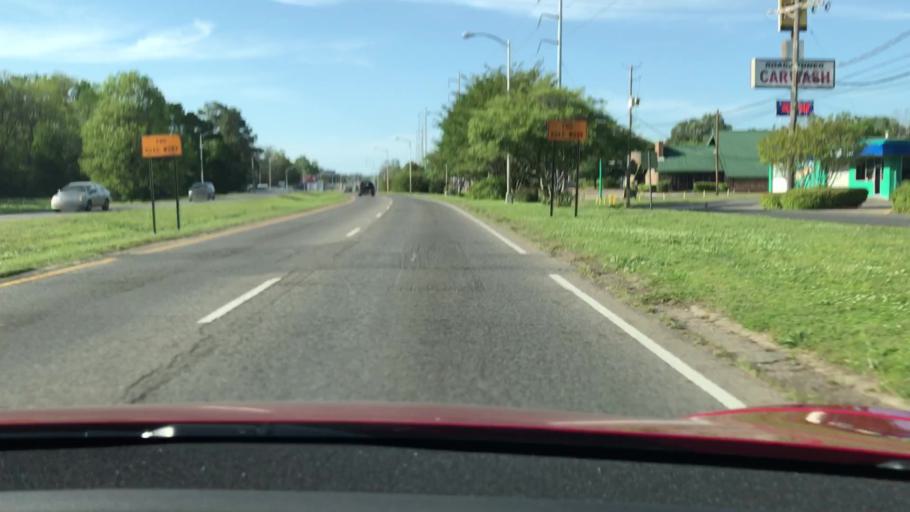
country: US
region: Louisiana
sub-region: Bossier Parish
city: Bossier City
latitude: 32.4860
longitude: -93.7240
